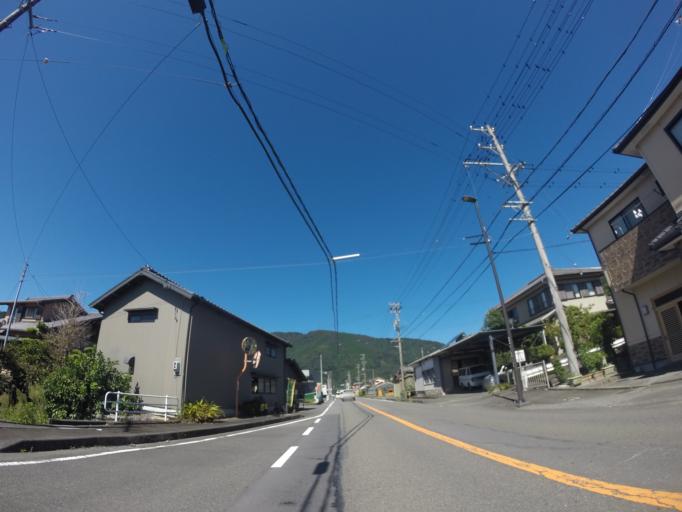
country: JP
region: Shizuoka
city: Kanaya
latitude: 34.8727
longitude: 138.1136
